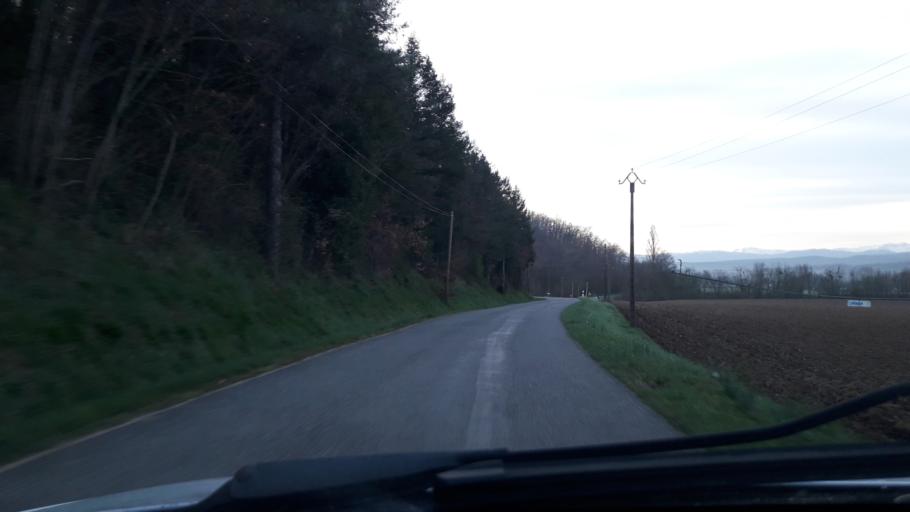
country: FR
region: Midi-Pyrenees
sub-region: Departement de la Haute-Garonne
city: Montesquieu-Volvestre
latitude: 43.1928
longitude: 1.2516
